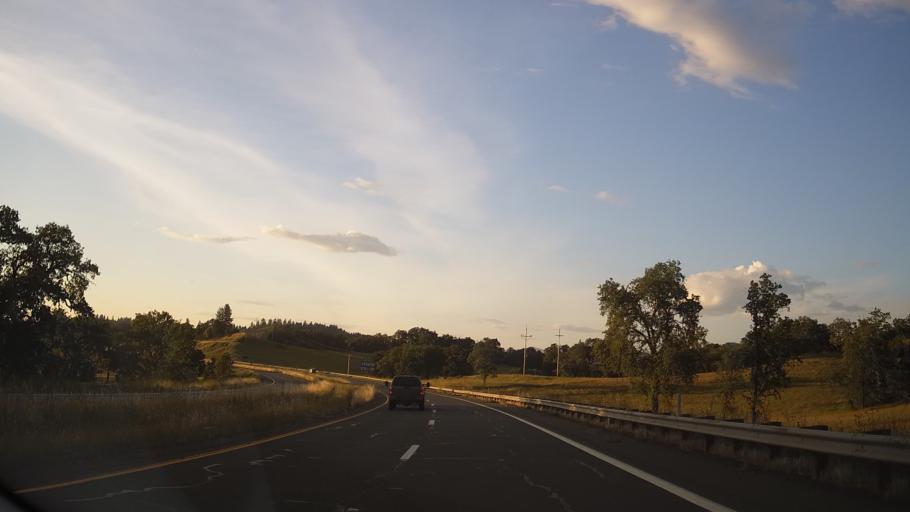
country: US
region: California
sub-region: Mendocino County
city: Willits
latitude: 39.3627
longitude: -123.3155
